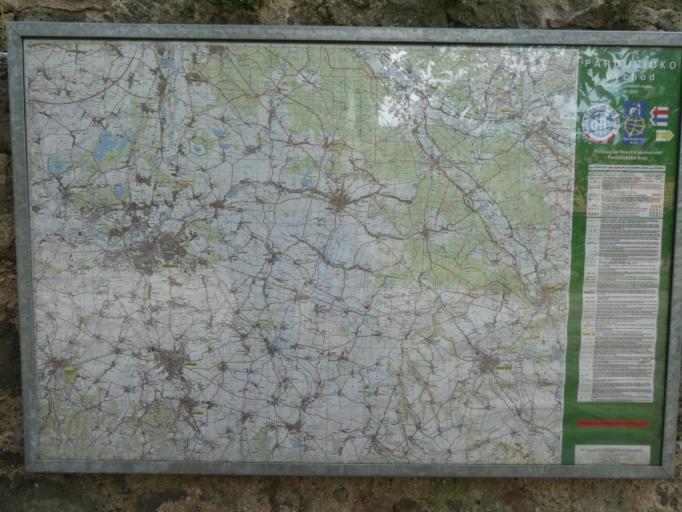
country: CZ
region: Pardubicky
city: Stare Hradiste
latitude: 50.0800
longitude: 15.8123
